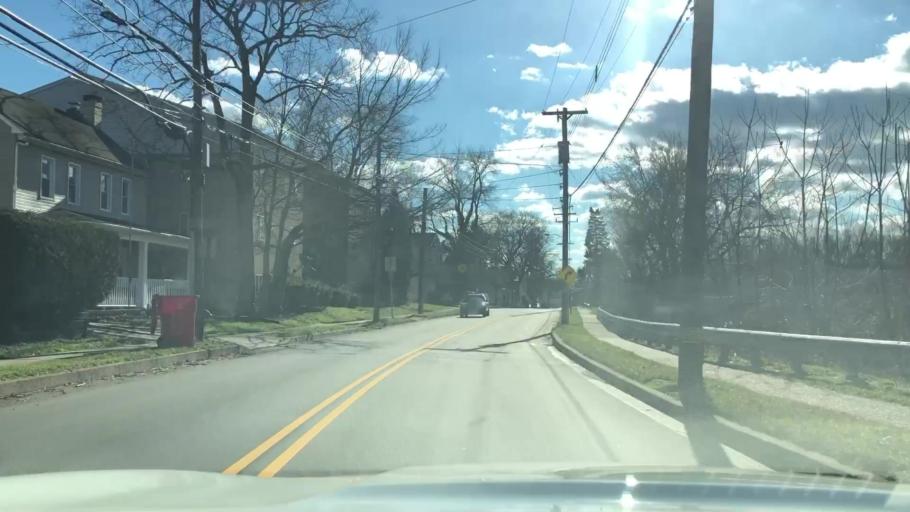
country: US
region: Pennsylvania
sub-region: Montgomery County
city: Pottstown
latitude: 40.2510
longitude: -75.6547
